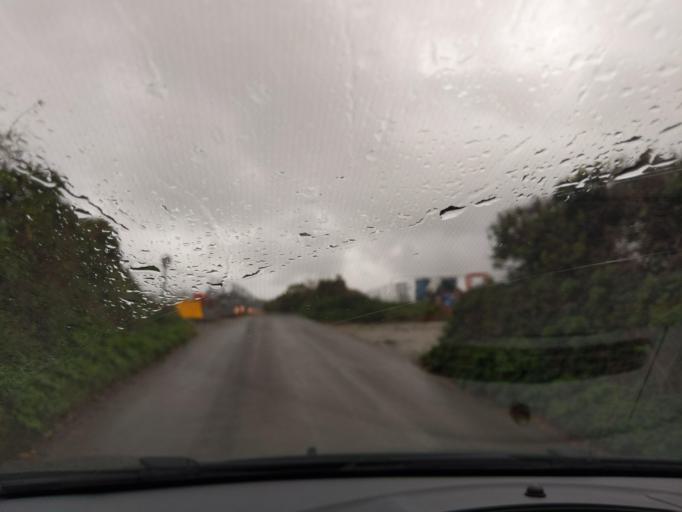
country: GB
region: England
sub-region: Cornwall
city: Wadebridge
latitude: 50.5169
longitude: -4.8209
